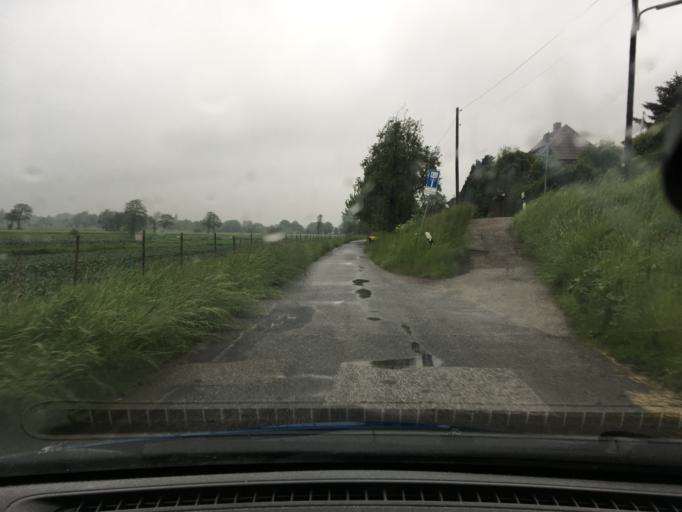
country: DE
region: Hamburg
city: Rothenburgsort
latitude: 53.4851
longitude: 10.0437
